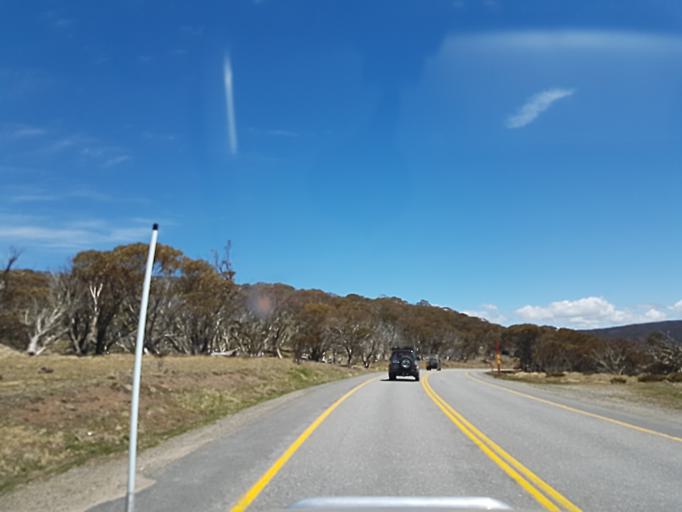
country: AU
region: Victoria
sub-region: Alpine
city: Mount Beauty
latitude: -37.0250
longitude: 147.2146
